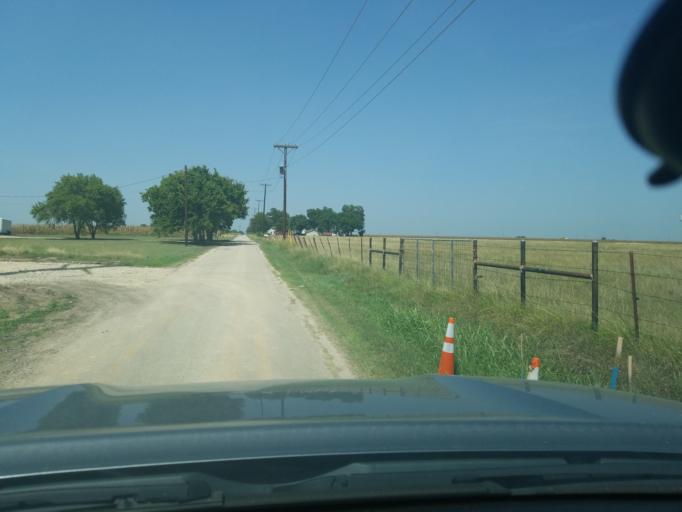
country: US
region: Texas
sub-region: Guadalupe County
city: Lake Dunlap
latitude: 29.6768
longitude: -98.0471
